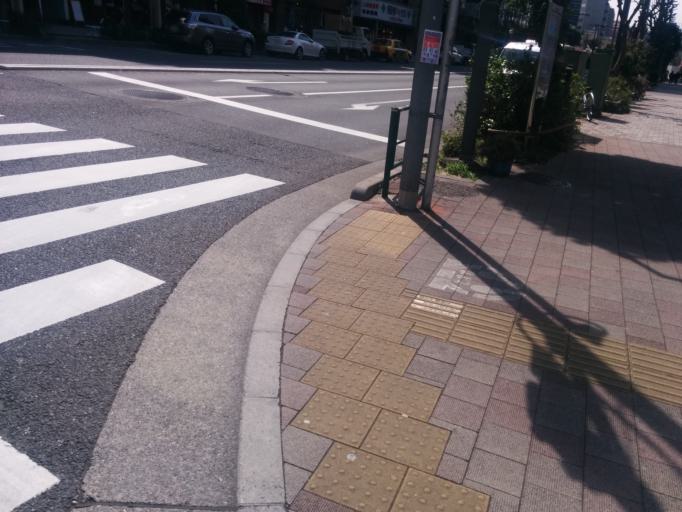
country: JP
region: Tokyo
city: Tokyo
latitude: 35.6958
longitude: 139.6886
